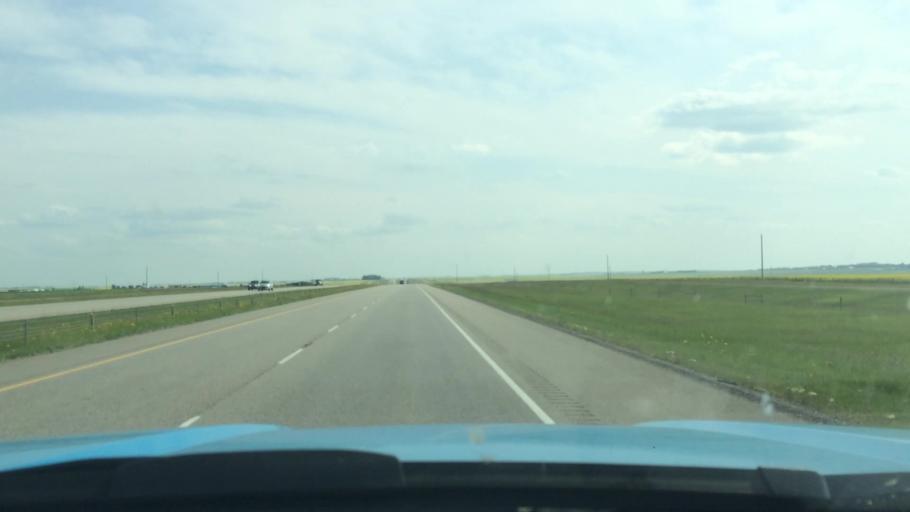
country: CA
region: Alberta
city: Carstairs
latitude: 51.6104
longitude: -114.0255
